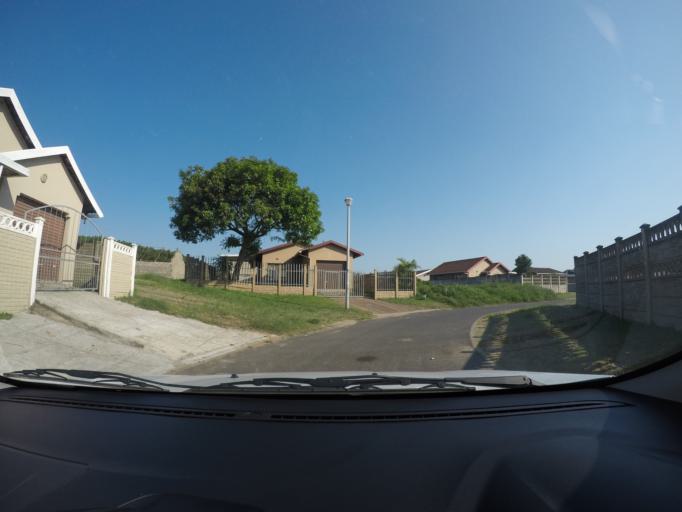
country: ZA
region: KwaZulu-Natal
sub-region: uThungulu District Municipality
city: Richards Bay
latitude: -28.7128
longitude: 32.0409
